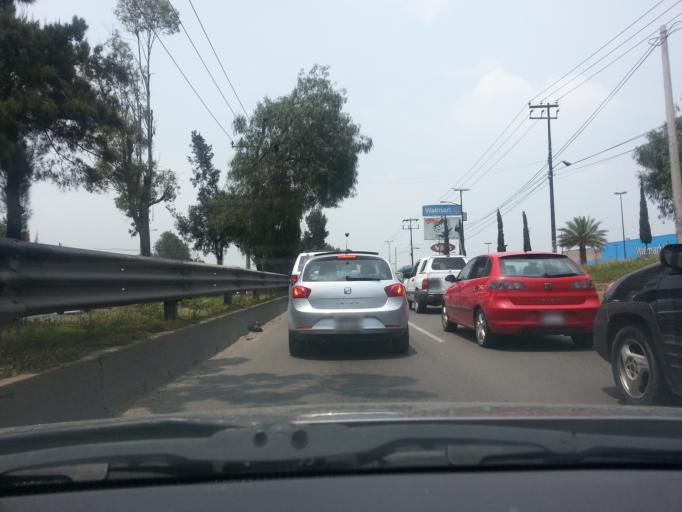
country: MX
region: Mexico
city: Cuautitlan Izcalli
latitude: 19.6451
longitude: -99.1957
